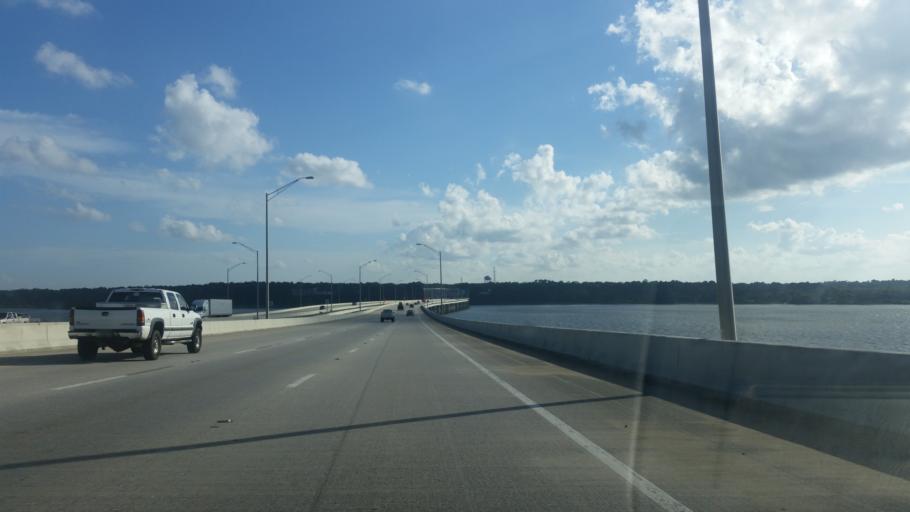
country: US
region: Florida
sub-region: Escambia County
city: Ferry Pass
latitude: 30.5137
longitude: -87.1520
